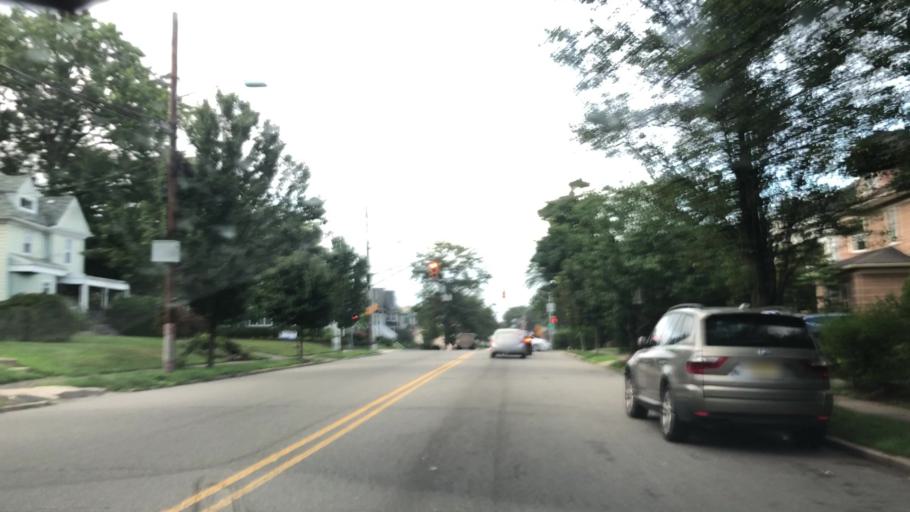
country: US
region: New Jersey
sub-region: Essex County
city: Glen Ridge
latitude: 40.8131
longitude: -74.2101
